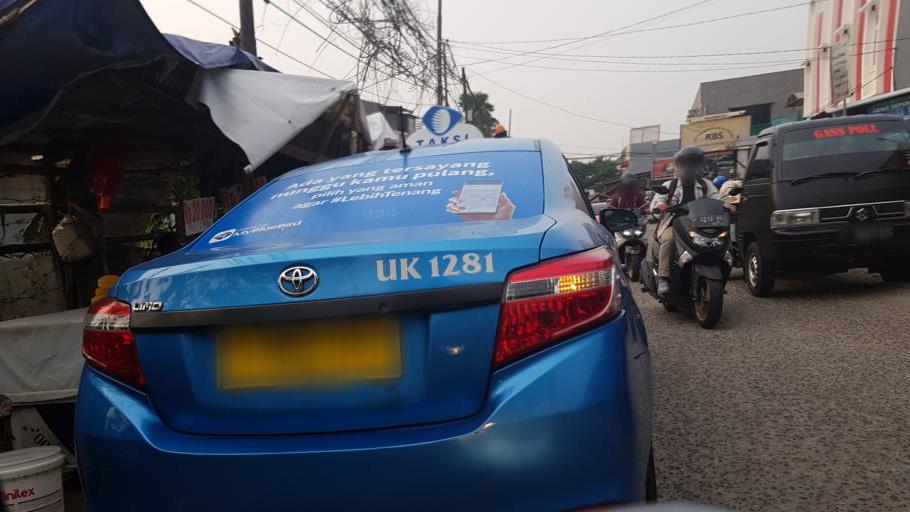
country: ID
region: West Java
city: Depok
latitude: -6.3711
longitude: 106.8426
